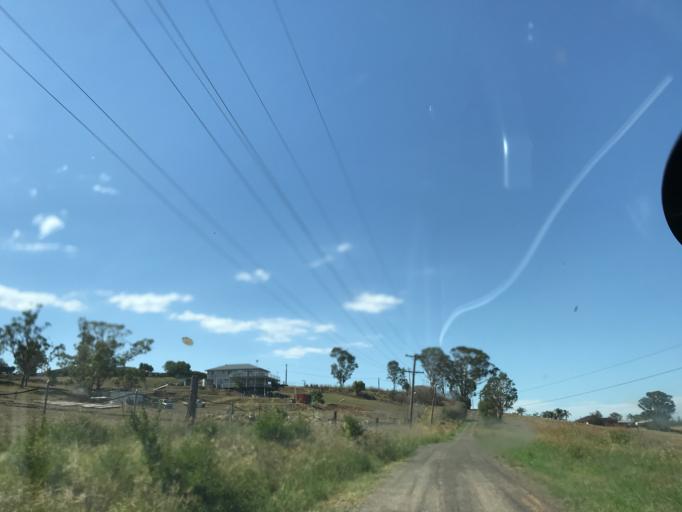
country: AU
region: New South Wales
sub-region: Penrith Municipality
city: Kingswood Park
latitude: -33.7950
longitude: 150.7371
